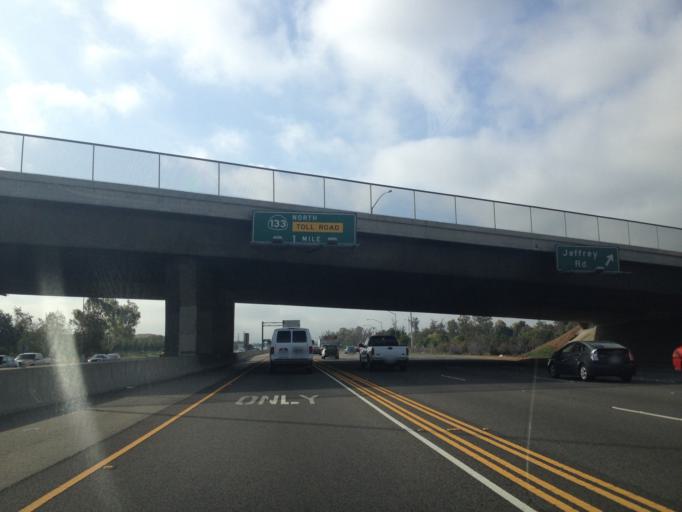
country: US
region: California
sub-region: Orange County
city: Irvine
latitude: 33.6904
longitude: -117.7689
